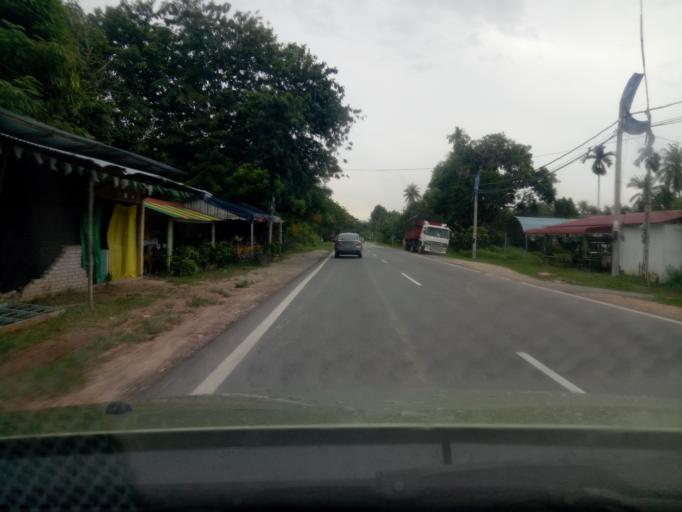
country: MY
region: Kedah
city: Gurun
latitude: 5.9697
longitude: 100.4334
